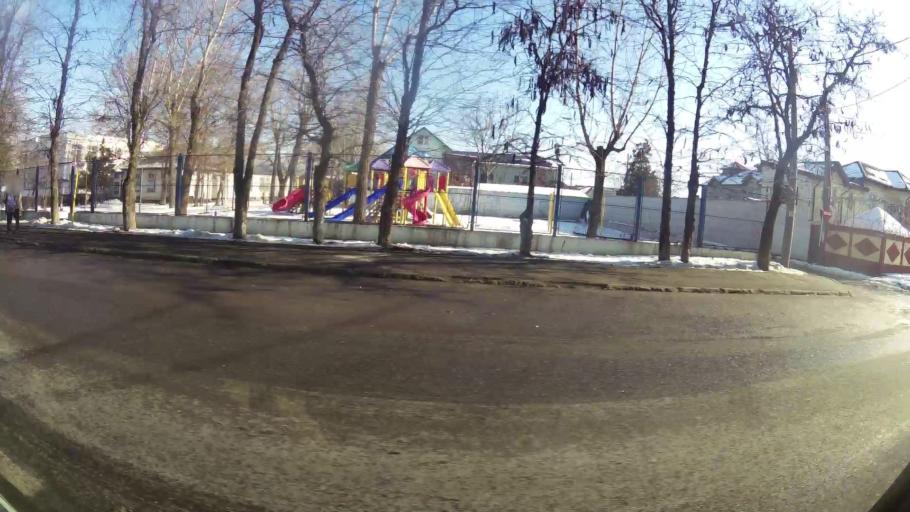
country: RO
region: Ilfov
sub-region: Comuna Magurele
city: Magurele
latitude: 44.3880
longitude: 26.0474
